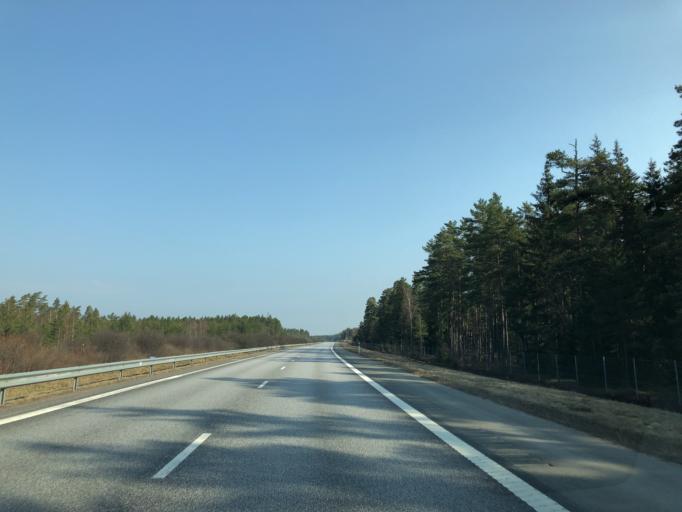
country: SE
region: Joenkoeping
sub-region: Varnamo Kommun
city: Varnamo
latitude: 57.2382
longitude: 14.0777
